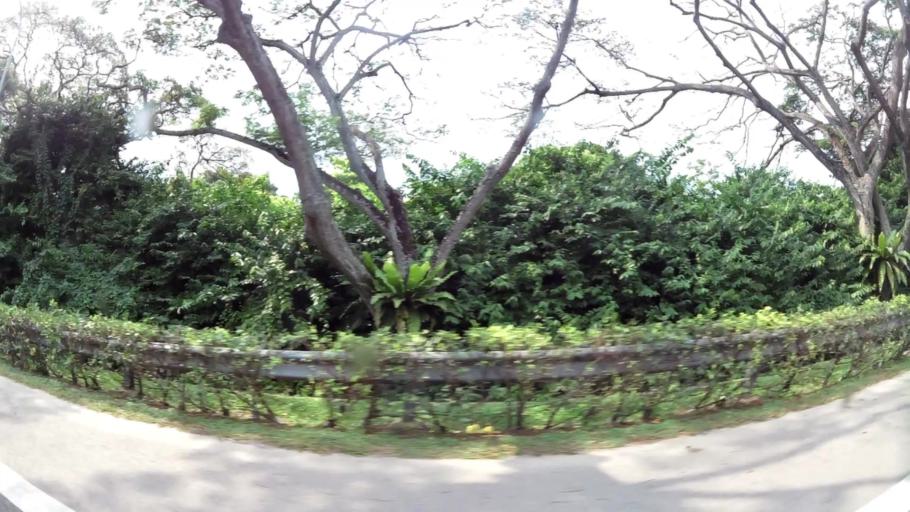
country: SG
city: Singapore
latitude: 1.3299
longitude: 103.9751
